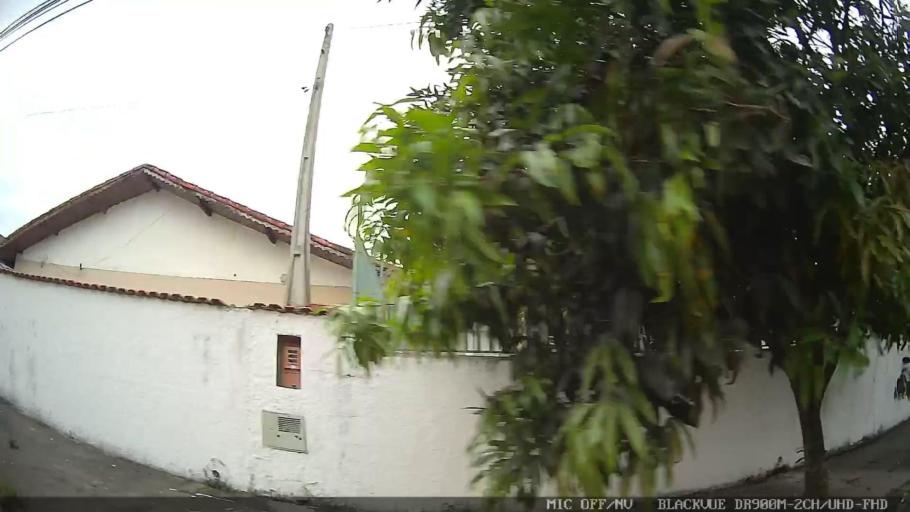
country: BR
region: Sao Paulo
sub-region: Peruibe
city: Peruibe
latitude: -24.3082
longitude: -46.9921
